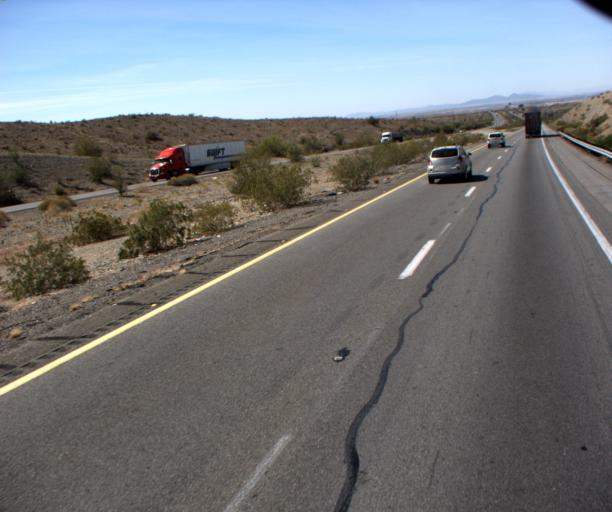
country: US
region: Arizona
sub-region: La Paz County
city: Ehrenberg
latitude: 33.6310
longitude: -114.4096
